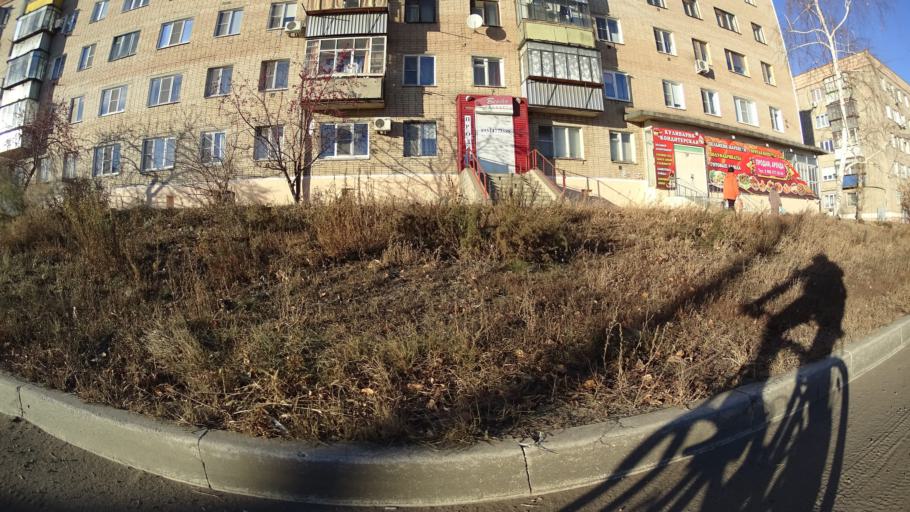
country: RU
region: Chelyabinsk
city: Troitsk
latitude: 54.0807
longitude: 61.5396
